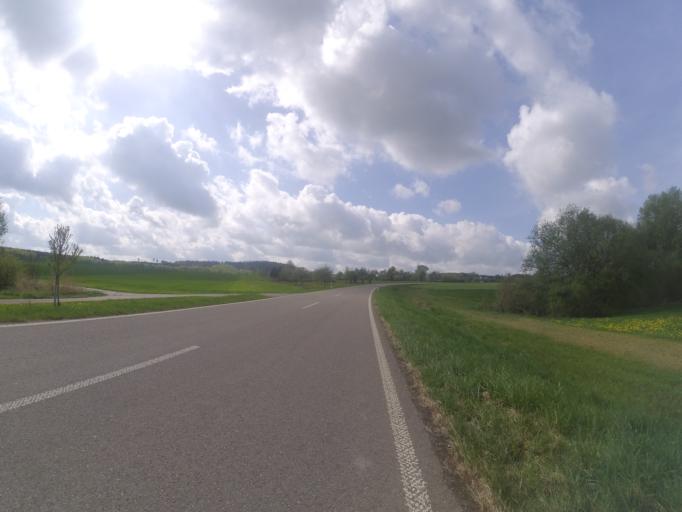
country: DE
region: Baden-Wuerttemberg
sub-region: Tuebingen Region
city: Griesingen
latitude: 48.2364
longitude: 9.7687
